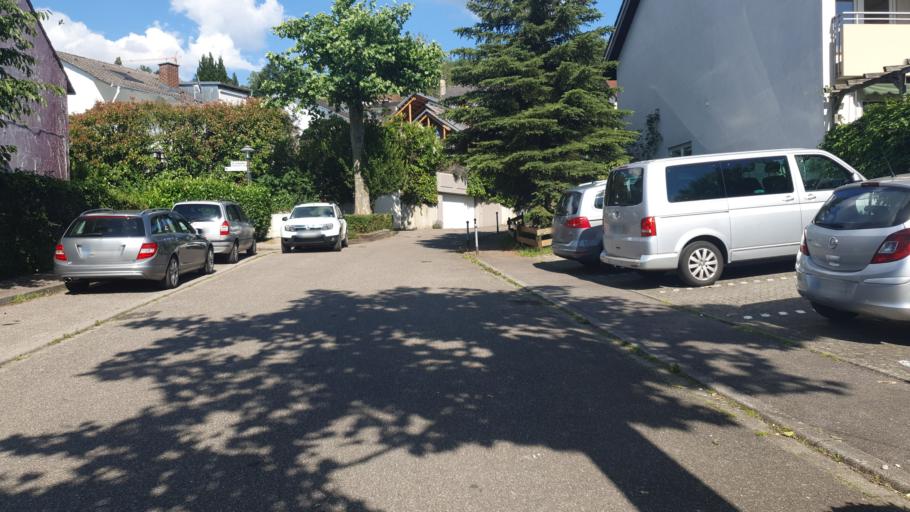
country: DE
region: Baden-Wuerttemberg
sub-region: Freiburg Region
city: Merzhausen
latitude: 47.9717
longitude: 7.8332
